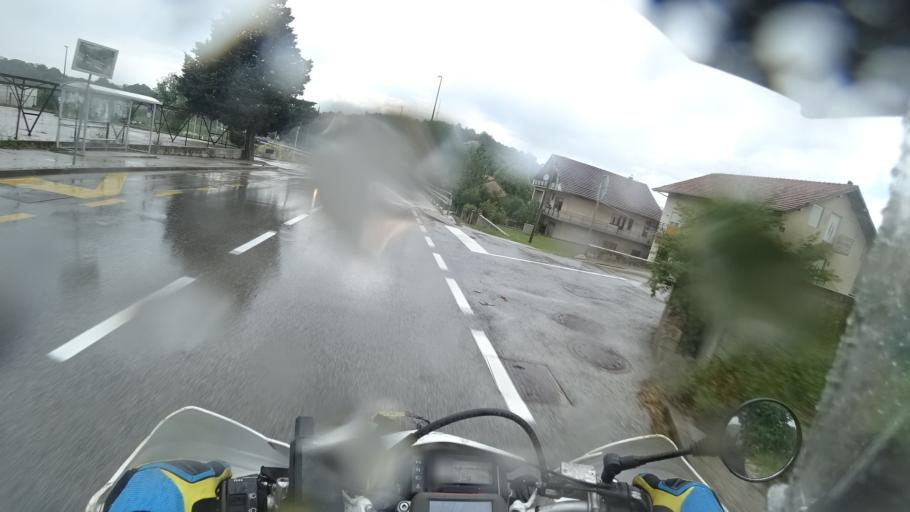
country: HR
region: Sibensko-Kniniska
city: Knin
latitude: 44.0446
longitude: 16.2155
